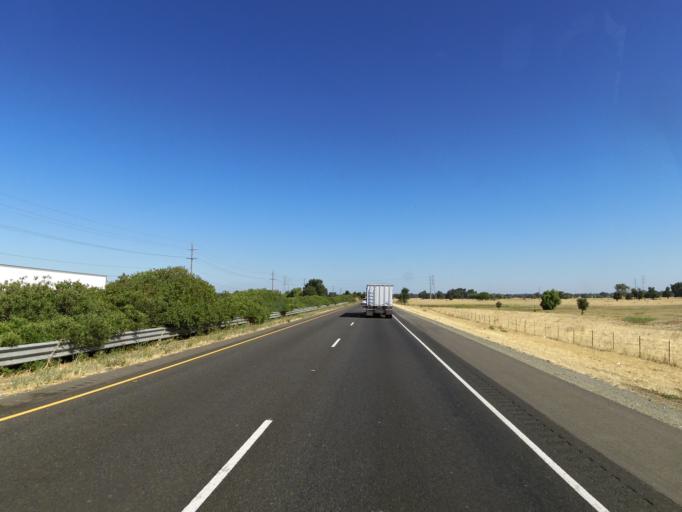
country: US
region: California
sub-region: Sacramento County
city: Galt
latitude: 38.3300
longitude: -121.3293
